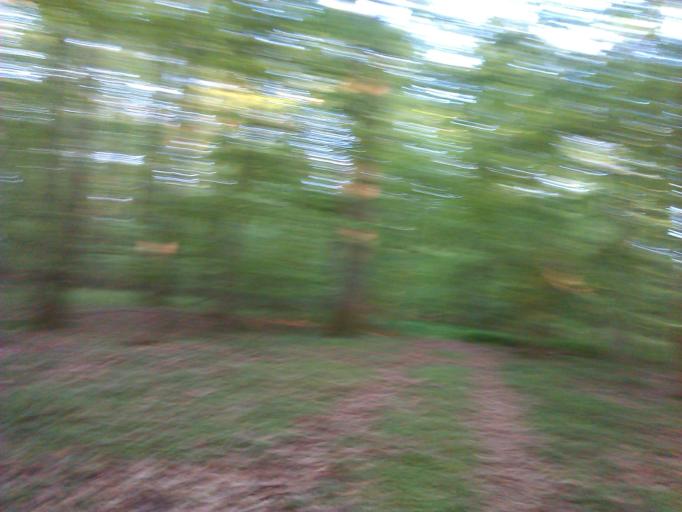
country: DE
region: Baden-Wuerttemberg
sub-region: Regierungsbezirk Stuttgart
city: Brackenheim
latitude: 49.1004
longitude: 9.0917
